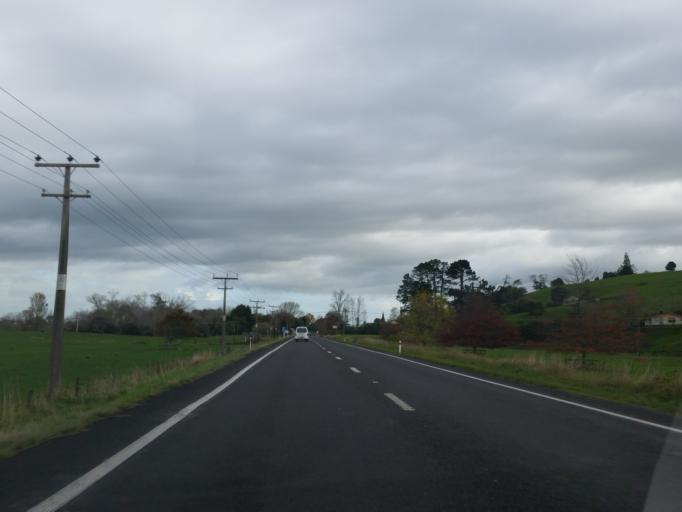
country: NZ
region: Waikato
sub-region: Hauraki District
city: Paeroa
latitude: -37.3894
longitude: 175.6840
